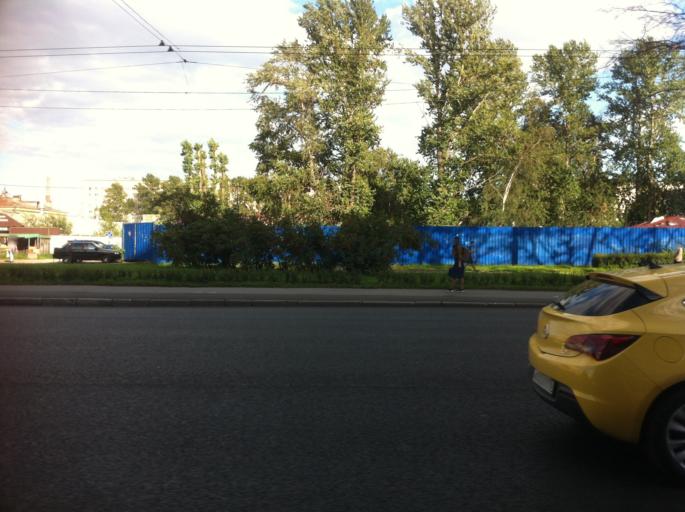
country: RU
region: St.-Petersburg
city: Avtovo
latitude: 59.8823
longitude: 30.2634
